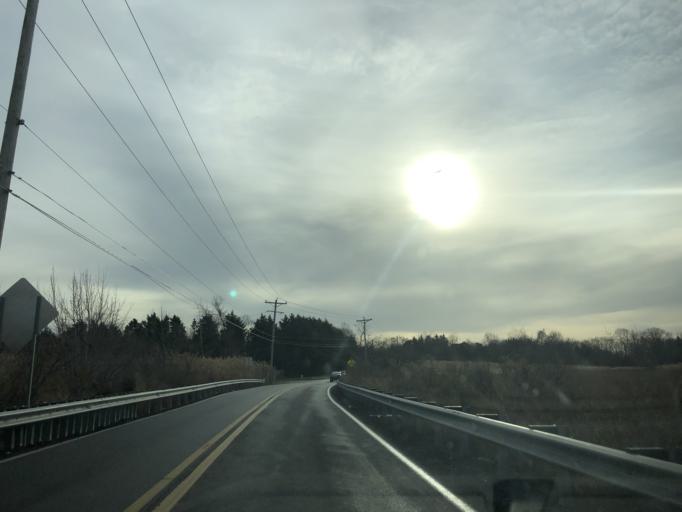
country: US
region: Delaware
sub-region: New Castle County
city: Middletown
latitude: 39.4508
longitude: -75.6514
